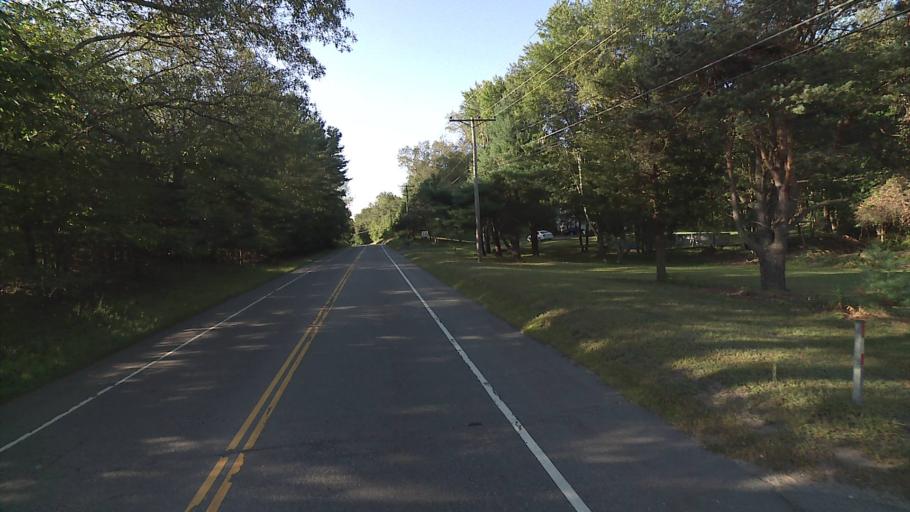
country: US
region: Connecticut
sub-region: Windham County
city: South Windham
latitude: 41.6641
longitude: -72.1604
